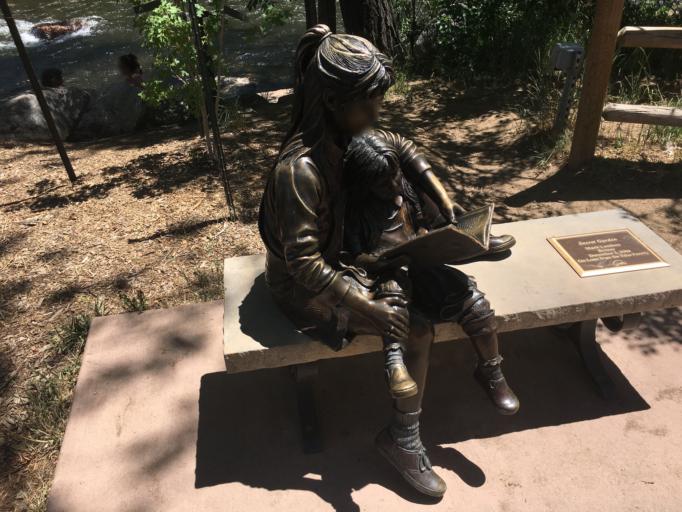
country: US
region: Colorado
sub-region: Jefferson County
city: Golden
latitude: 39.7554
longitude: -105.2256
